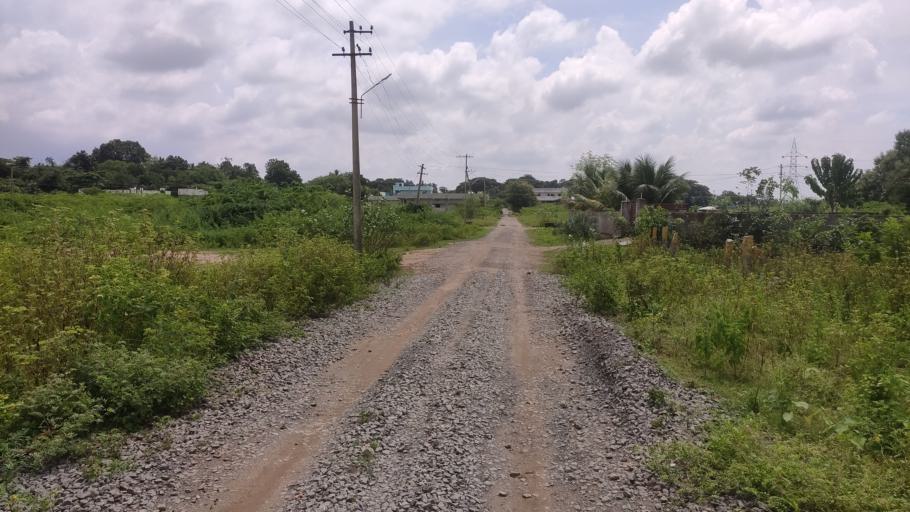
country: IN
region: Telangana
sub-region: Khammam
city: Khammam
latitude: 17.2451
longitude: 80.1935
